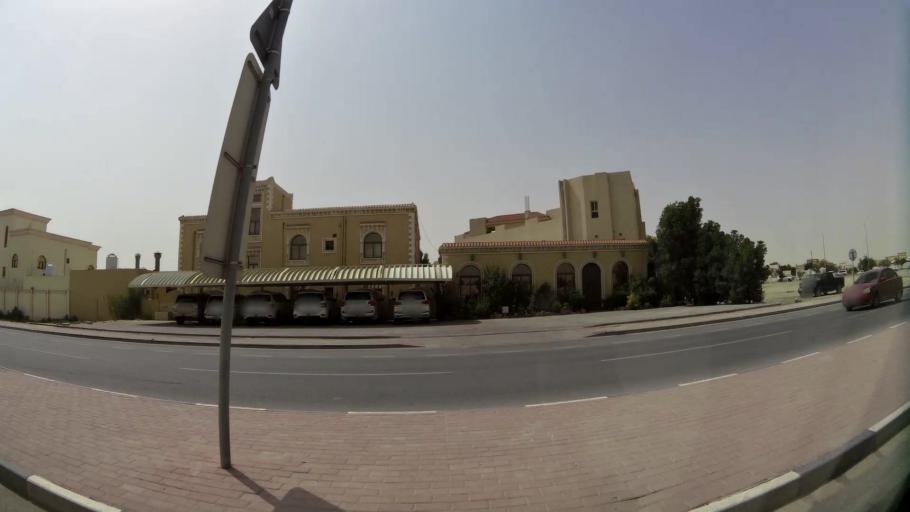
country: QA
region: Baladiyat ar Rayyan
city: Ar Rayyan
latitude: 25.2448
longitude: 51.4204
